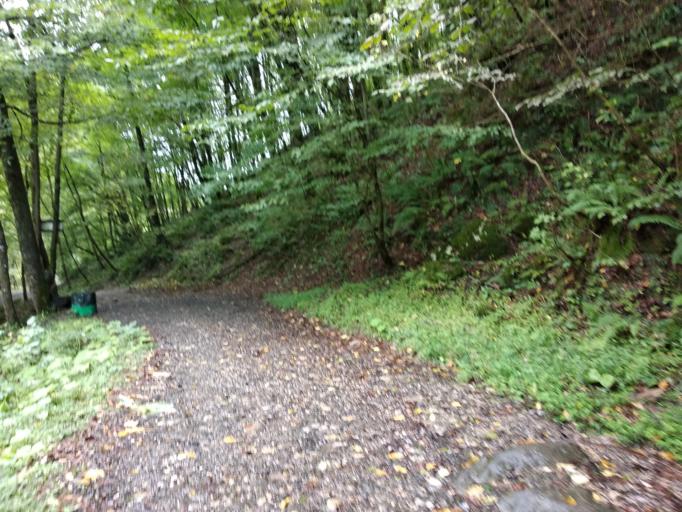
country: RU
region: Krasnodarskiy
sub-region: Sochi City
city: Sochi
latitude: 43.6383
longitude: 39.8113
